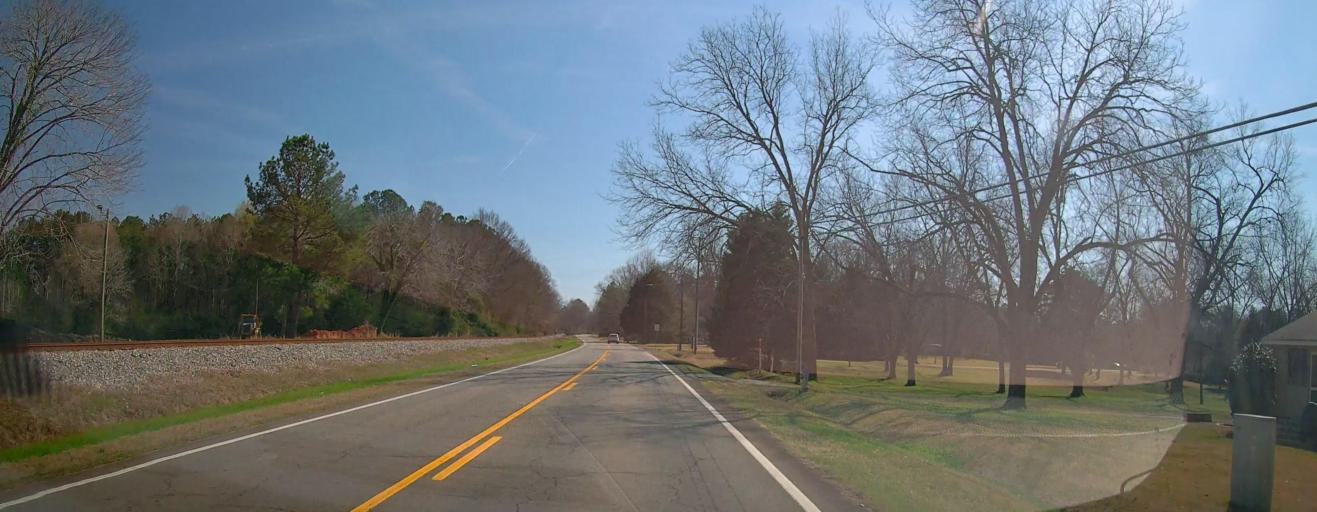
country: US
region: Georgia
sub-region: Jones County
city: Gray
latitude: 33.0191
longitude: -83.5361
